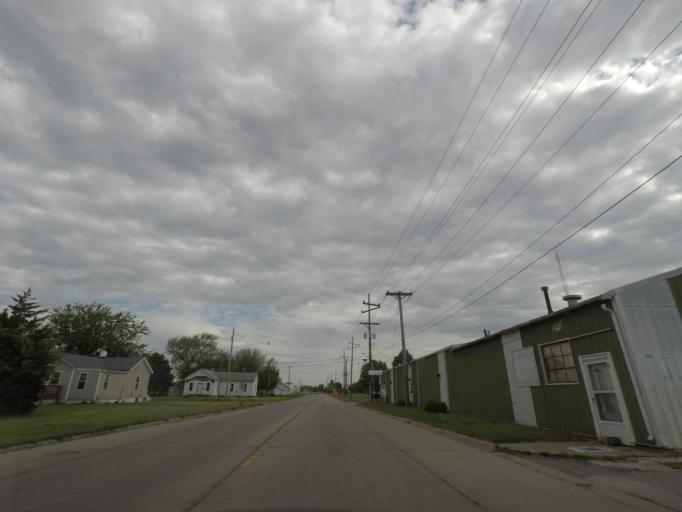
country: US
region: Illinois
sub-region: Logan County
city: Lincoln
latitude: 40.1430
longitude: -89.3488
